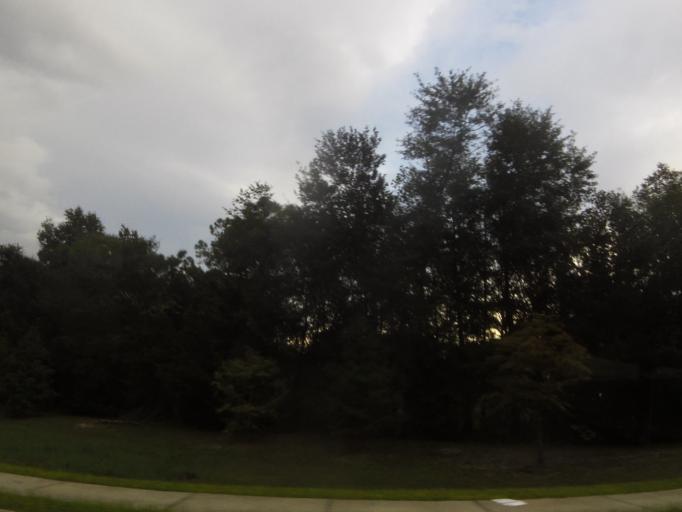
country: US
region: Florida
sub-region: Clay County
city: Bellair-Meadowbrook Terrace
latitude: 30.2845
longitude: -81.8028
